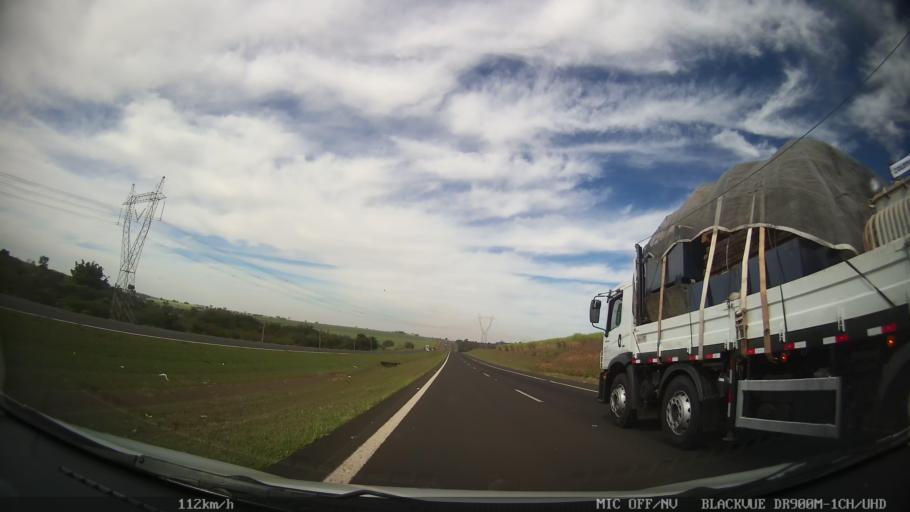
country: BR
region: Sao Paulo
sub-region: Matao
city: Matao
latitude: -21.5478
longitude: -48.4939
